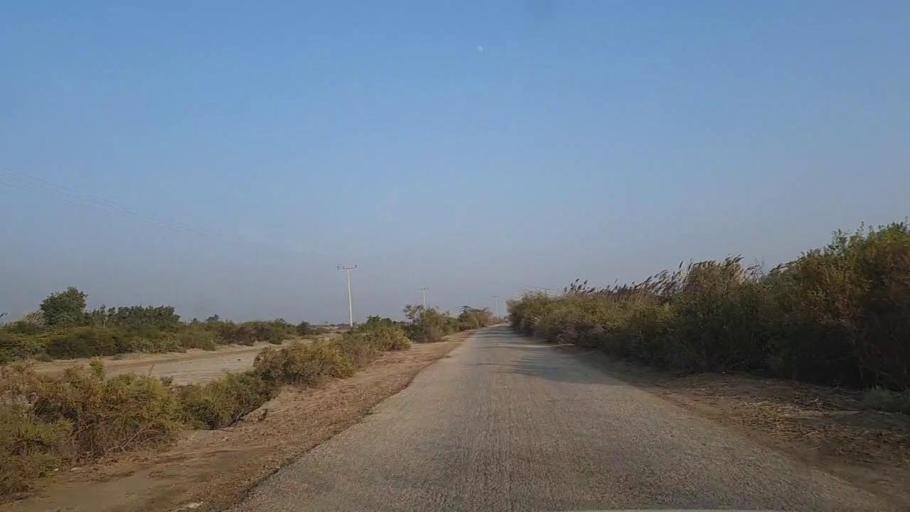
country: PK
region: Sindh
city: Keti Bandar
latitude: 24.2801
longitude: 67.6276
